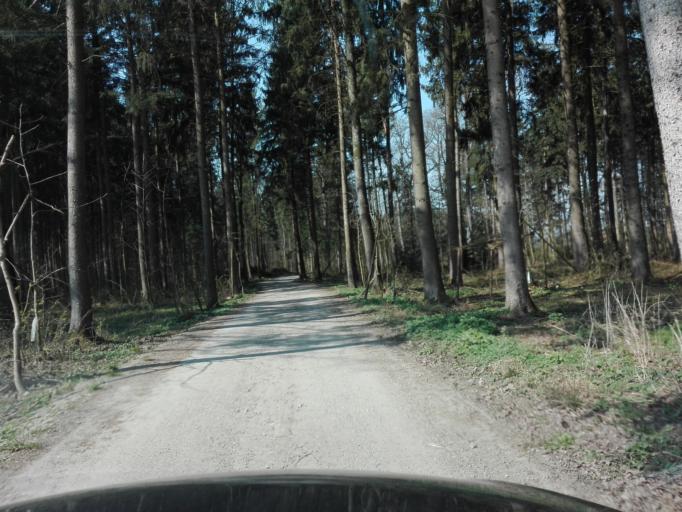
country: AT
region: Upper Austria
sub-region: Politischer Bezirk Perg
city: Perg
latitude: 48.2064
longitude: 14.6721
